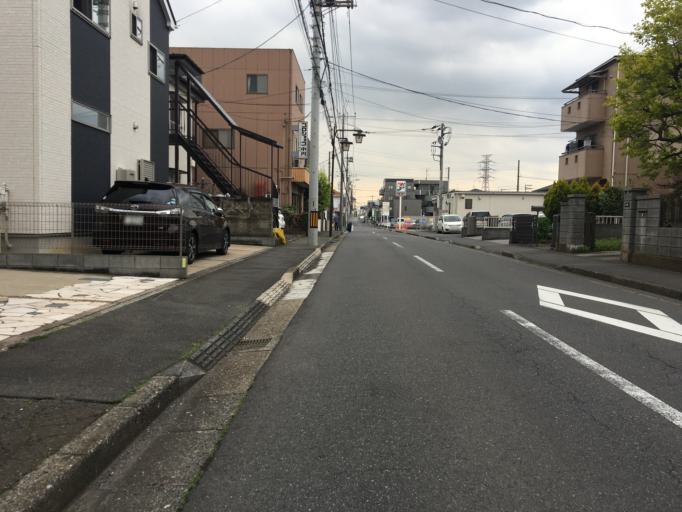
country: JP
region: Saitama
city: Shiki
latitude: 35.8427
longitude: 139.5519
